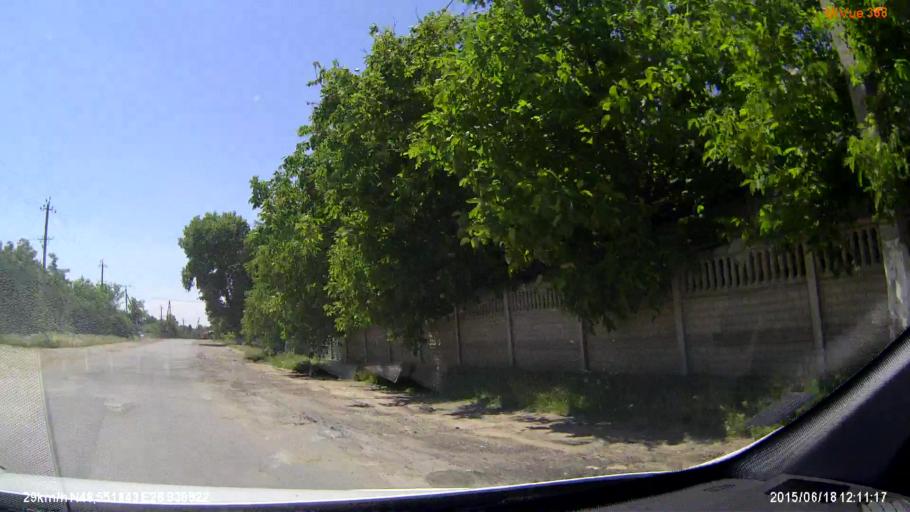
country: MD
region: Cimislia
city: Cimislia
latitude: 46.5517
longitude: 28.9307
